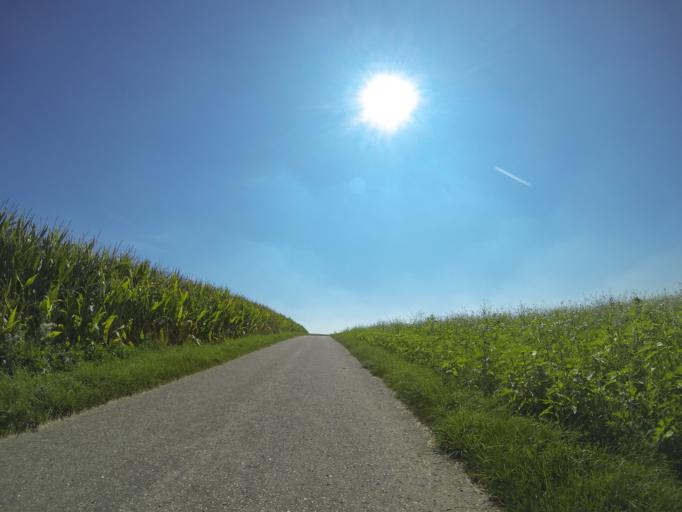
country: DE
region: Baden-Wuerttemberg
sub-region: Tuebingen Region
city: Achstetten
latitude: 48.2525
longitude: 9.9196
